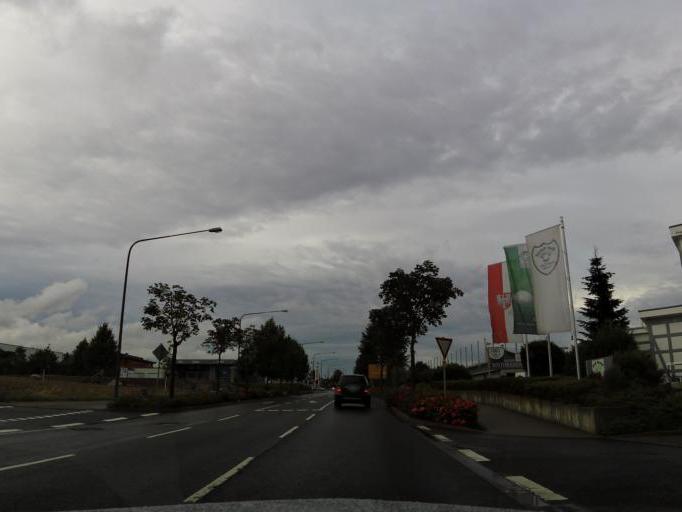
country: DE
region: Hesse
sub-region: Regierungsbezirk Darmstadt
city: Bad Homburg vor der Hoehe
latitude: 50.1876
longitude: 8.6508
